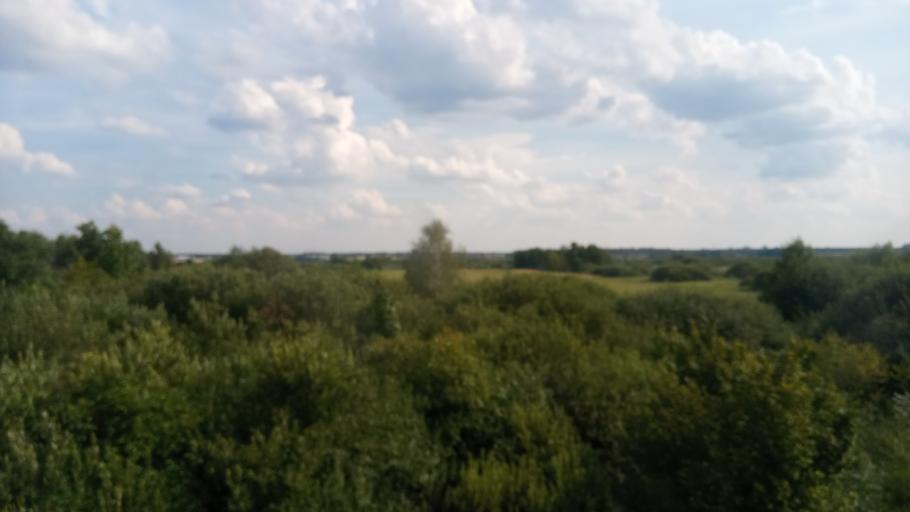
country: PL
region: Kujawsko-Pomorskie
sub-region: Powiat bydgoski
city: Biale Blota
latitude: 53.1528
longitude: 17.8674
